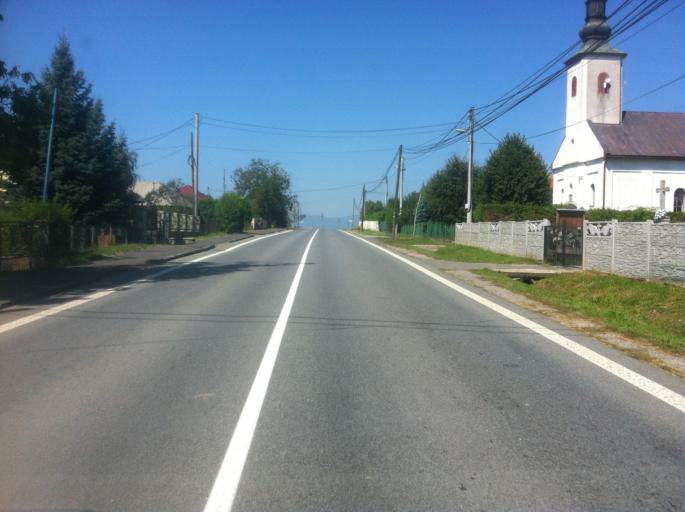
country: SK
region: Kosicky
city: Sobrance
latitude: 48.7094
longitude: 22.2226
